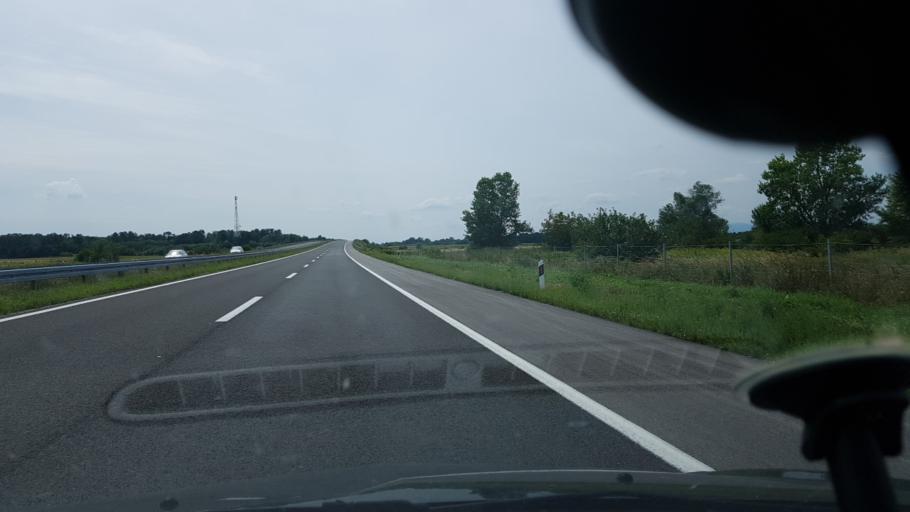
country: HR
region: Medimurska
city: Palovec
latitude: 46.3820
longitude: 16.5550
